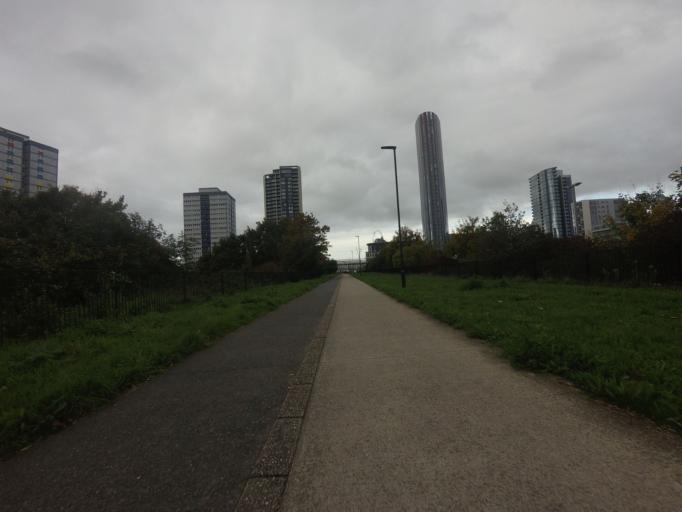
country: GB
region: England
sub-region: Greater London
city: Poplar
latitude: 51.5330
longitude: -0.0042
